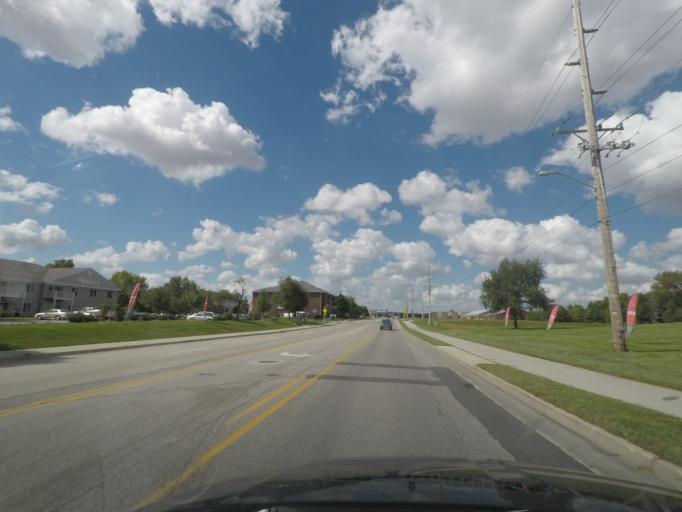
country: US
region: Iowa
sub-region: Story County
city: Ames
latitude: 42.0121
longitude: -93.6751
